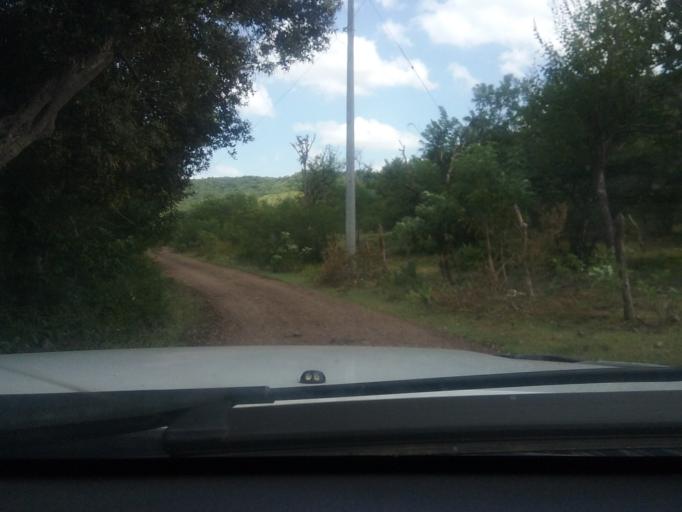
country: NI
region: Matagalpa
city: Terrabona
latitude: 12.6525
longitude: -86.0010
